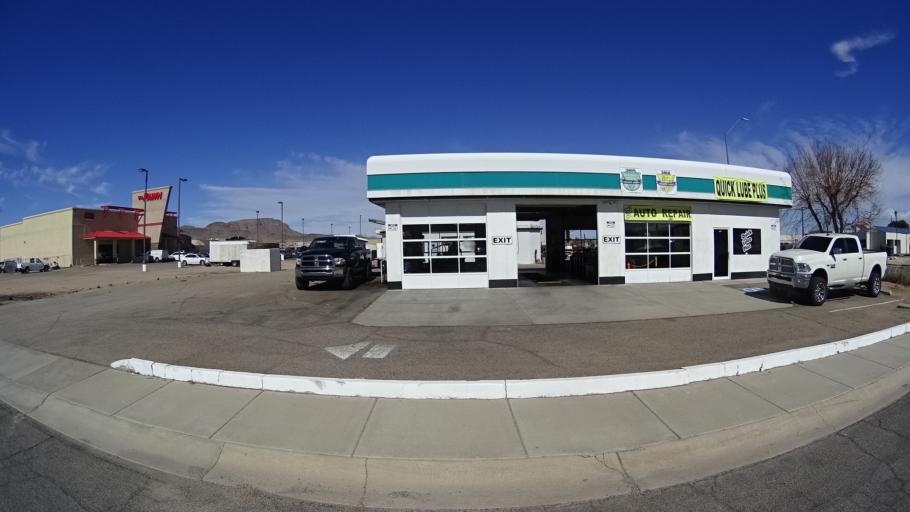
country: US
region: Arizona
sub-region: Mohave County
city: Kingman
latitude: 35.2132
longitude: -114.0355
